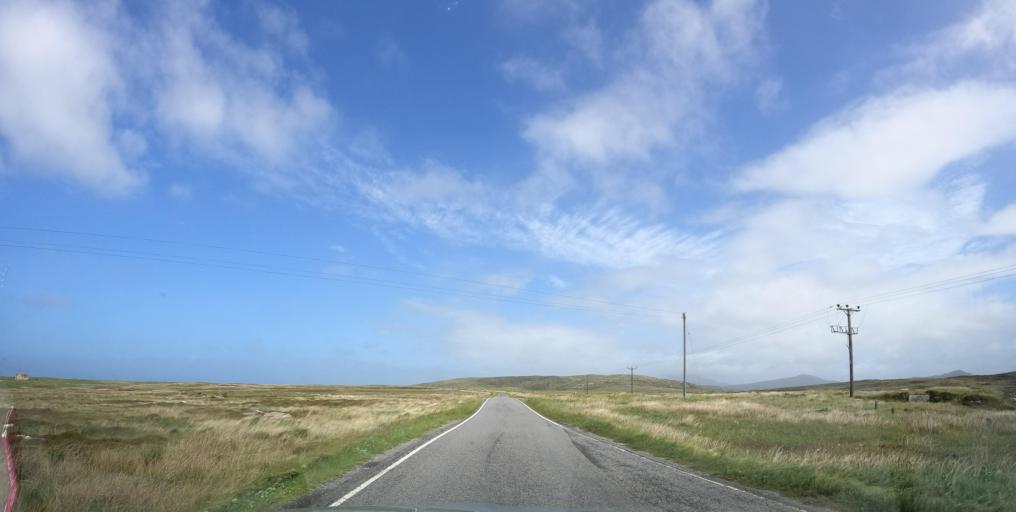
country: GB
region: Scotland
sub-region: Eilean Siar
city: Isle of South Uist
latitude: 57.1298
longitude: -7.3609
